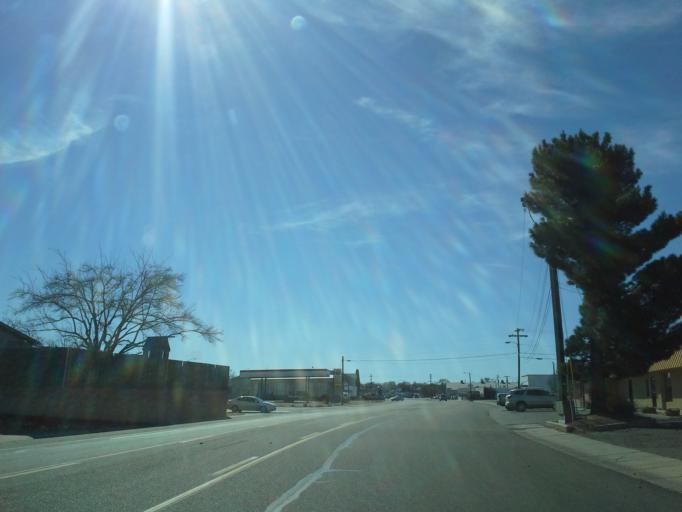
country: US
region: Arizona
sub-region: Coconino County
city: Page
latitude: 36.9223
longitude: -111.4573
